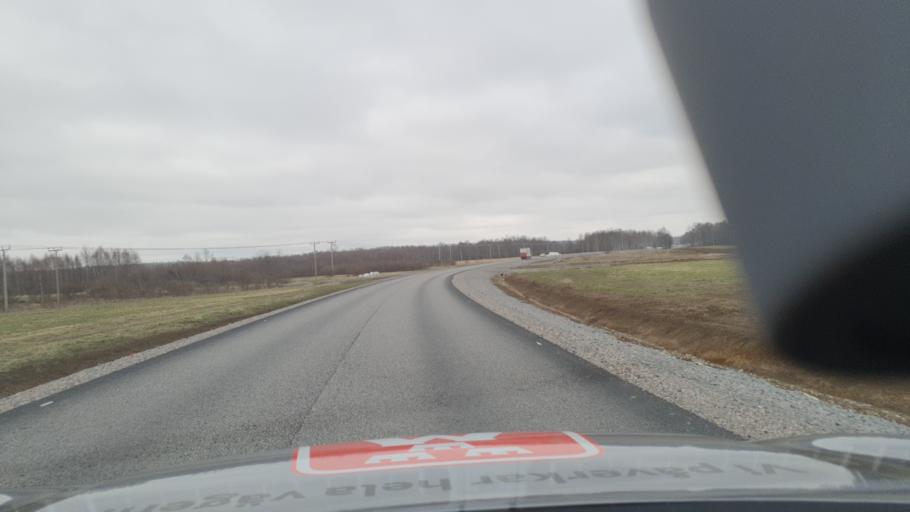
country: SE
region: Norrbotten
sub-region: Kalix Kommun
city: Rolfs
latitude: 65.8832
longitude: 23.0567
